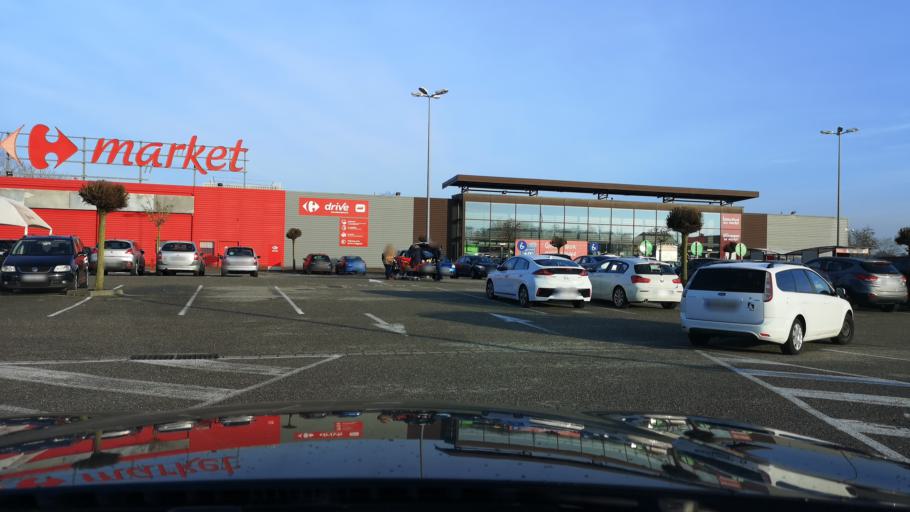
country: DE
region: Rheinland-Pfalz
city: Scheibenhardt
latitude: 48.9749
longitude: 8.1578
